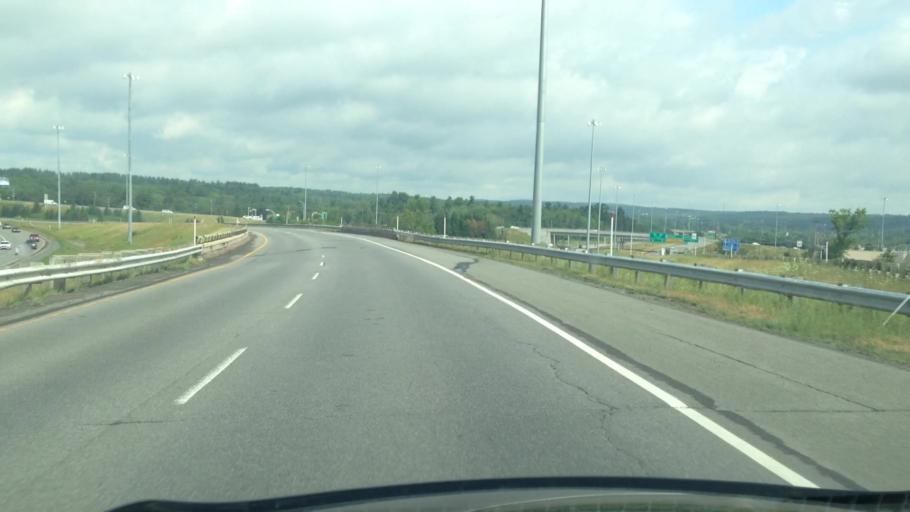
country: CA
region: Quebec
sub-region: Laurentides
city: Saint-Jerome
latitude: 45.7922
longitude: -74.0205
